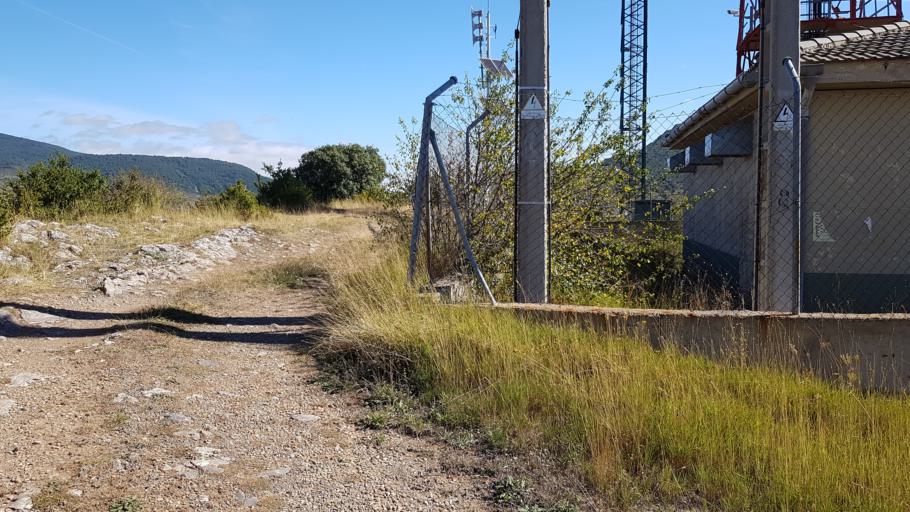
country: ES
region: La Rioja
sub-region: Provincia de La Rioja
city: Torrecilla en Cameros
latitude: 42.2503
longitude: -2.6203
